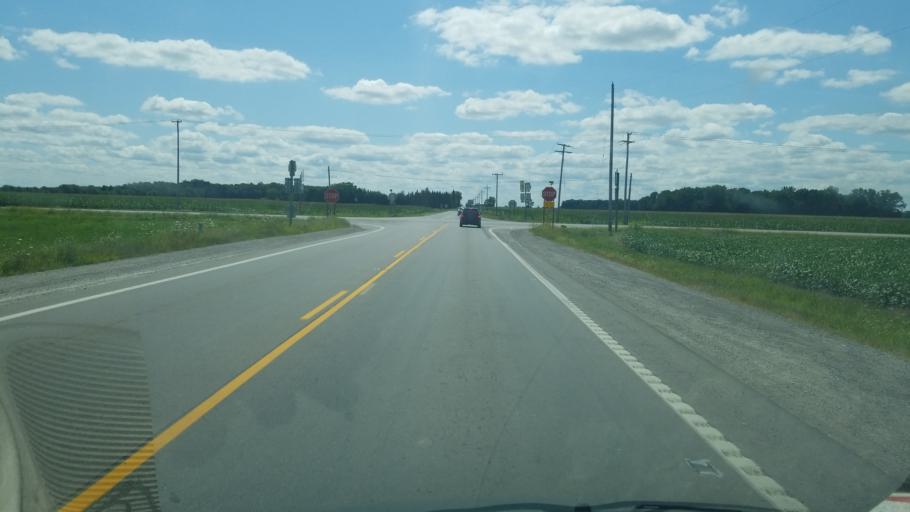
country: US
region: Ohio
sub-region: Fulton County
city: Delta
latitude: 41.6722
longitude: -84.0359
